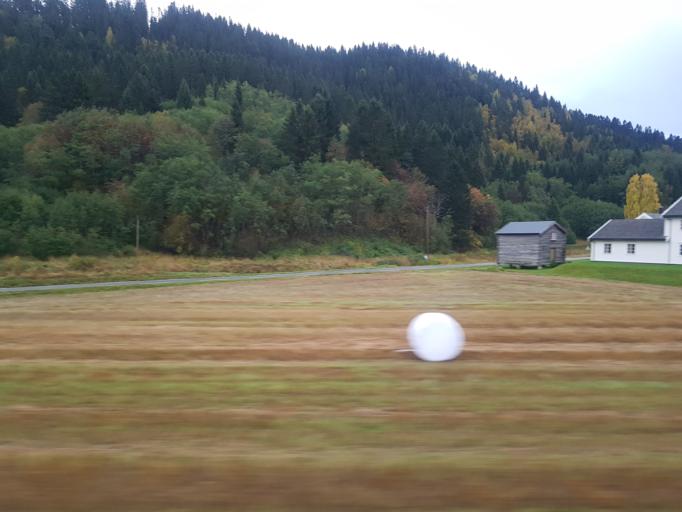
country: NO
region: Sor-Trondelag
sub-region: Melhus
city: Melhus
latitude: 63.2219
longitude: 10.2865
